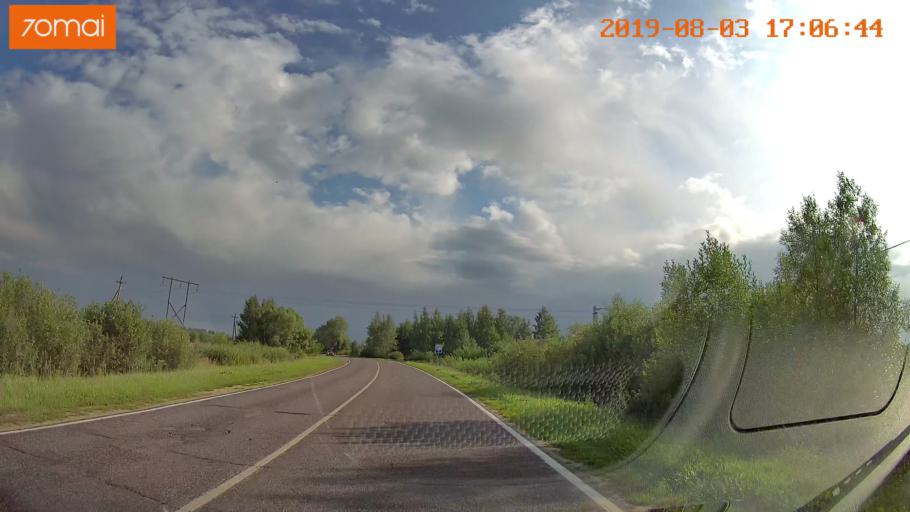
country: RU
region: Moskovskaya
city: Troitskoye
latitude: 55.3047
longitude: 38.5487
